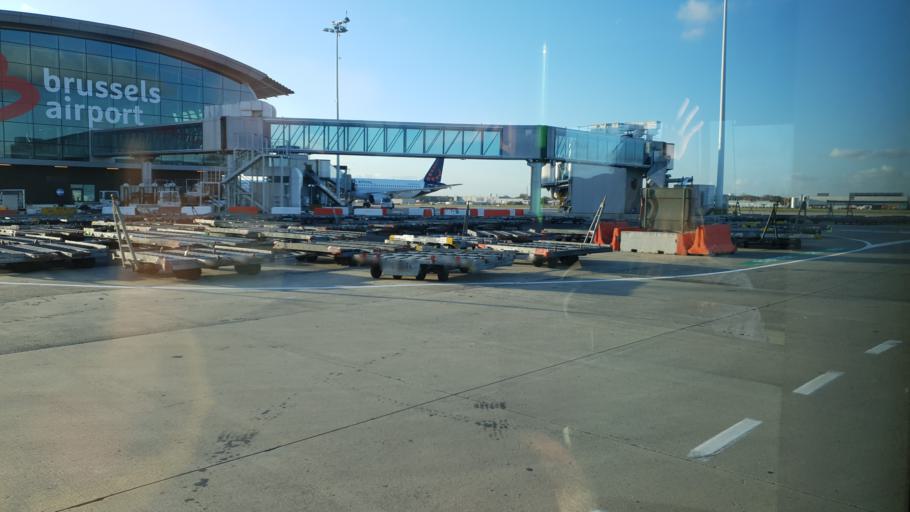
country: BE
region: Flanders
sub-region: Provincie Vlaams-Brabant
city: Steenokkerzeel
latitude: 50.9048
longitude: 4.4916
